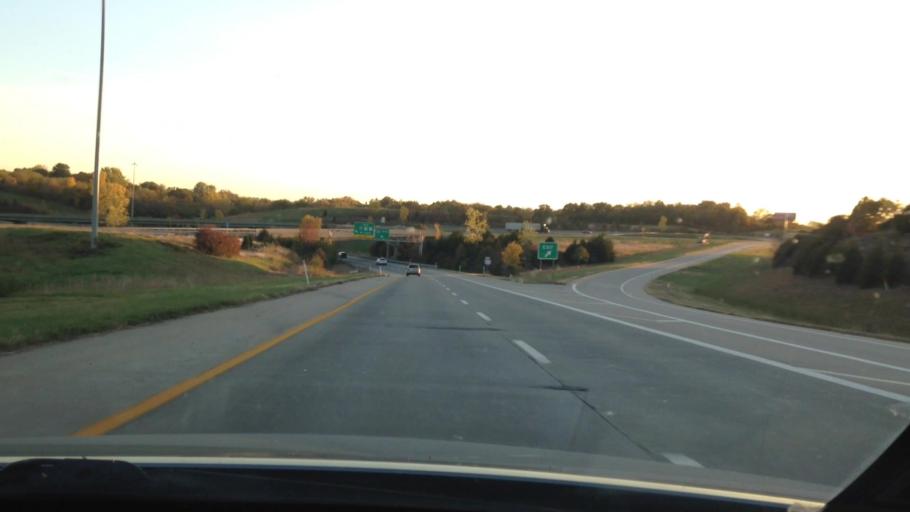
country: US
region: Kansas
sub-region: Wyandotte County
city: Edwardsville
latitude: 39.1100
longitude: -94.8140
